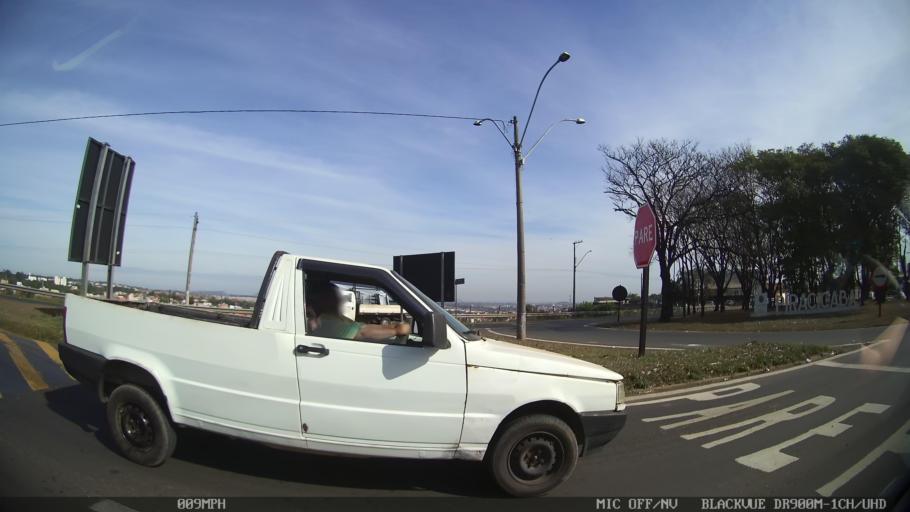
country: BR
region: Sao Paulo
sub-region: Piracicaba
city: Piracicaba
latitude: -22.7584
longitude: -47.6456
